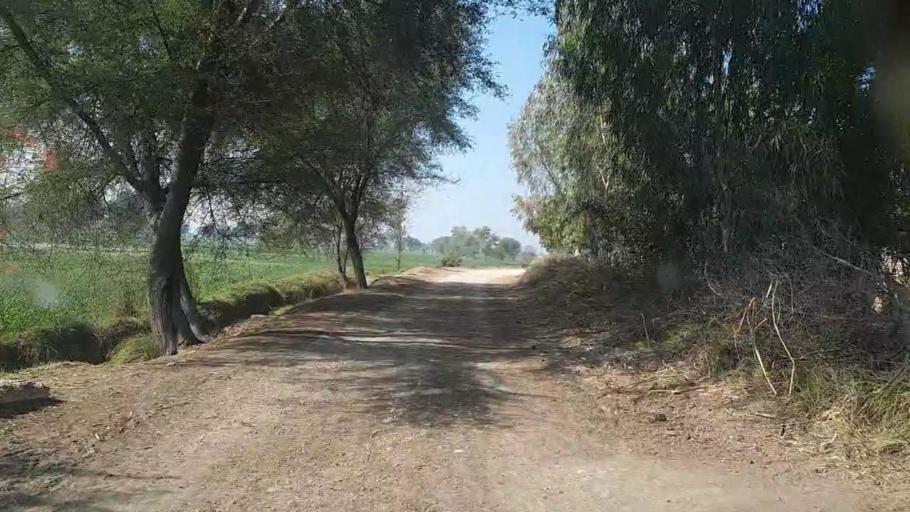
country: PK
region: Sindh
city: Khairpur
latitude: 27.9827
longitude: 69.6914
